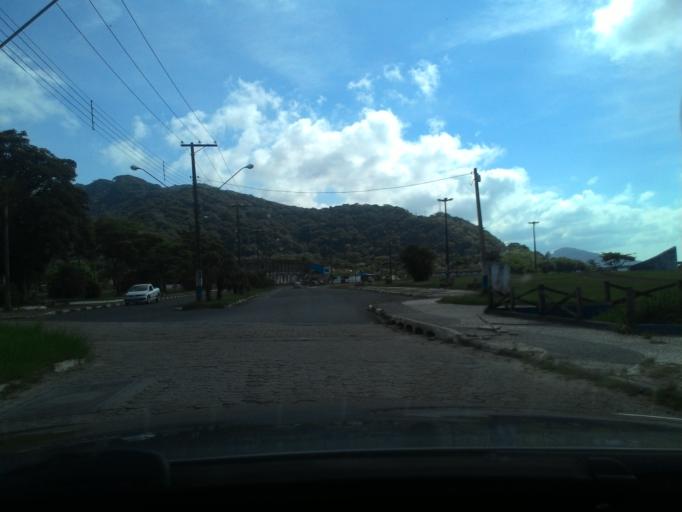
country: BR
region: Sao Paulo
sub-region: Iguape
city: Iguape
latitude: -24.7088
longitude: -47.5536
